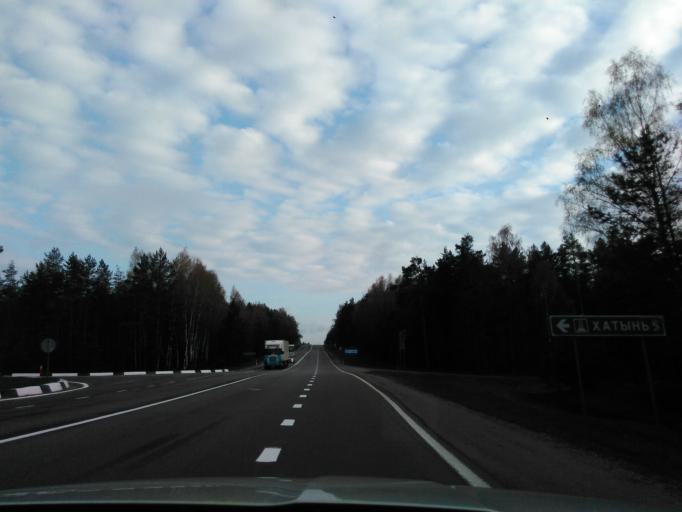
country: BY
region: Minsk
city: Plyeshchanitsy
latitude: 54.3279
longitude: 27.8753
